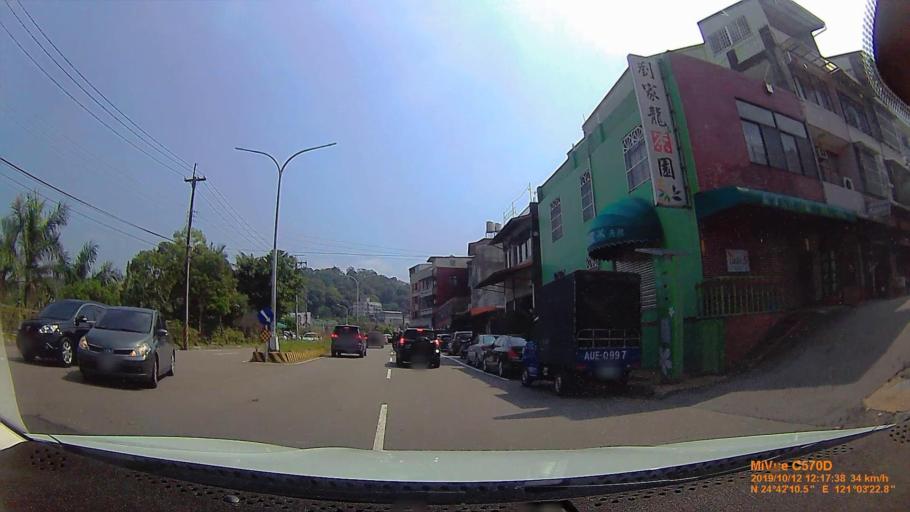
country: TW
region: Taiwan
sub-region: Hsinchu
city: Hsinchu
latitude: 24.7029
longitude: 121.0563
